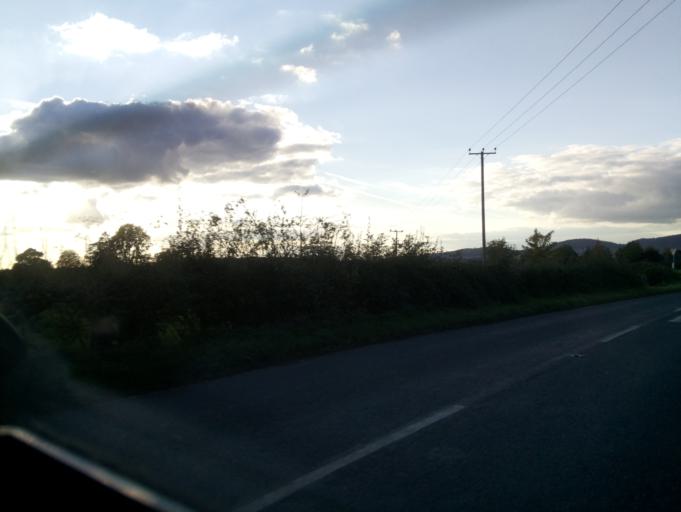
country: GB
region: England
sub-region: Worcestershire
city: Upton upon Severn
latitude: 52.0054
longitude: -2.2700
